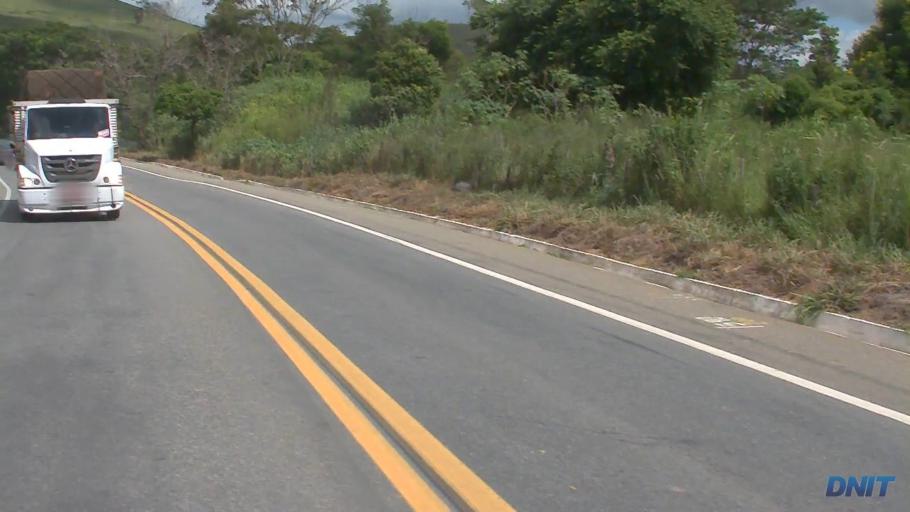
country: BR
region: Minas Gerais
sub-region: Governador Valadares
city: Governador Valadares
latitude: -18.9315
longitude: -42.0467
